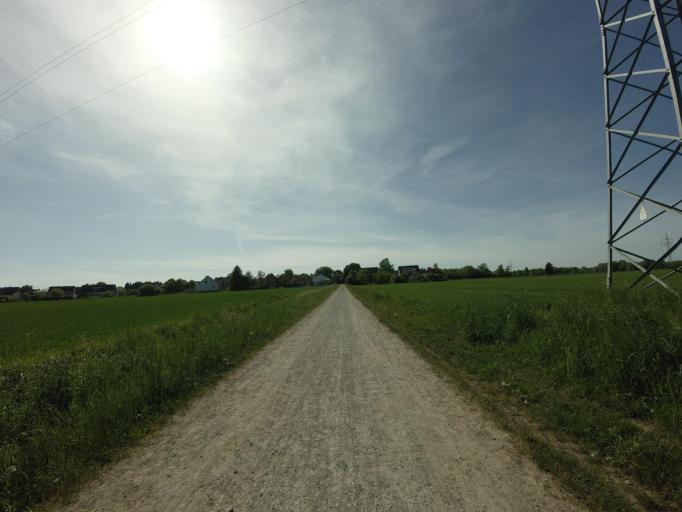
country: DE
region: Lower Saxony
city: Cremlingen
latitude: 52.2925
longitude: 10.6068
